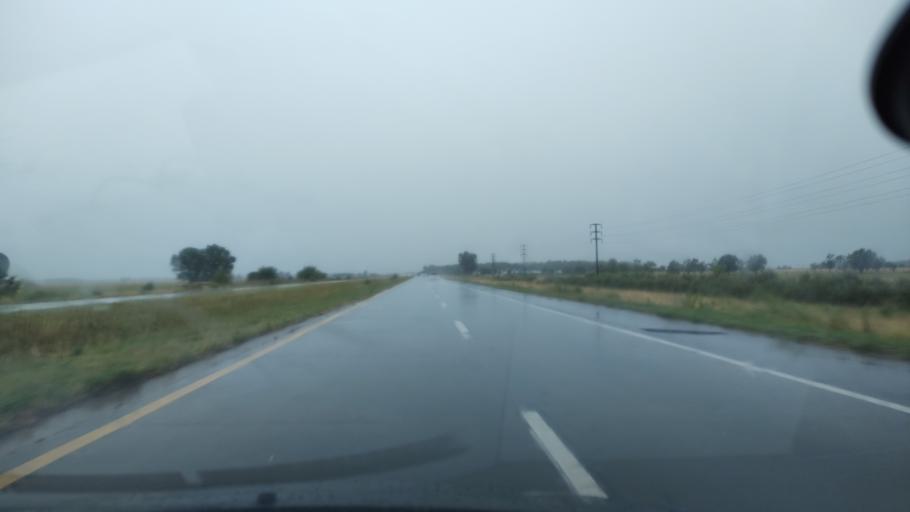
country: AR
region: Buenos Aires
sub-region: Partido de San Vicente
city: San Vicente
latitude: -35.0678
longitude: -58.5008
